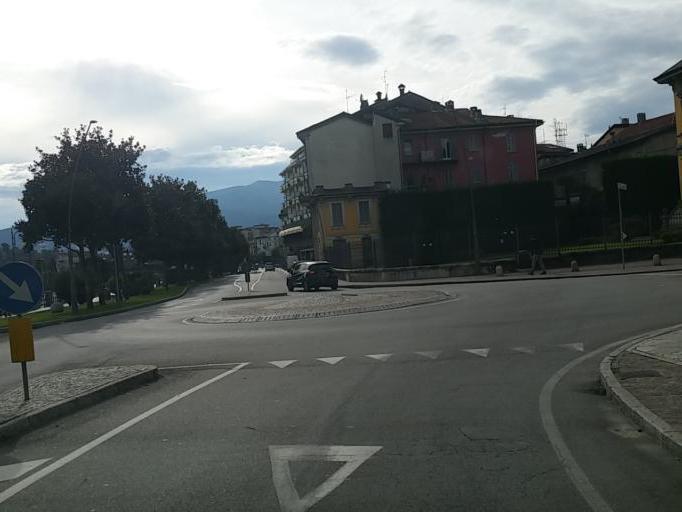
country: IT
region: Piedmont
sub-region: Provincia Verbano-Cusio-Ossola
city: Pallanza-Intra-Suna
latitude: 45.9370
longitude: 8.5779
